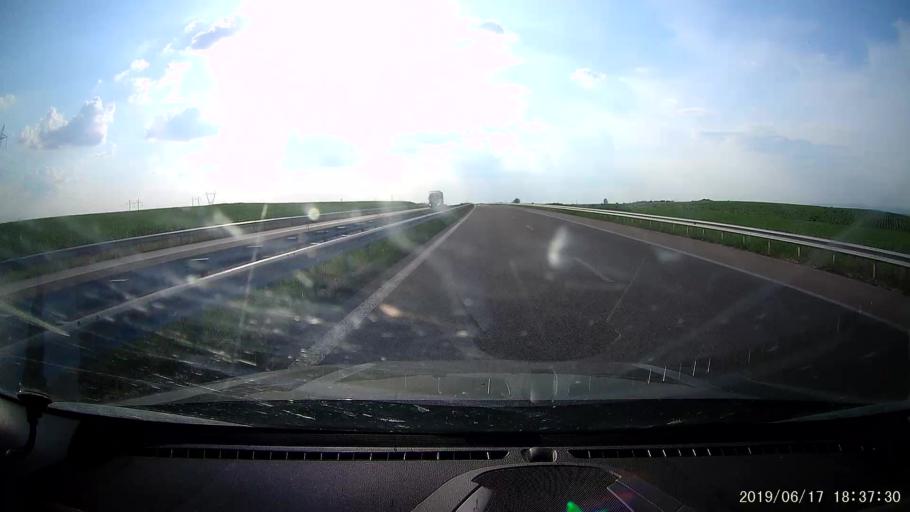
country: BG
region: Stara Zagora
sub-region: Obshtina Chirpan
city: Chirpan
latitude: 42.1311
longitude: 25.3591
